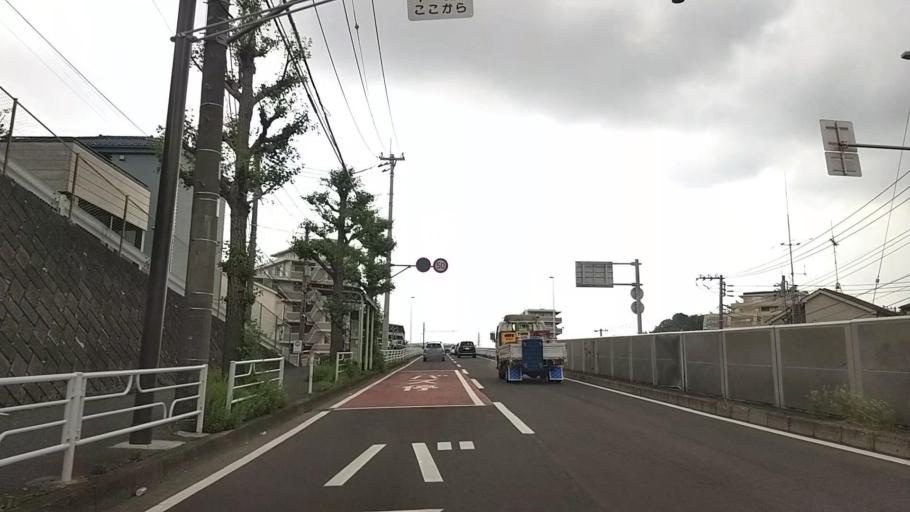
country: JP
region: Kanagawa
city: Yokohama
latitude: 35.4947
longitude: 139.6074
